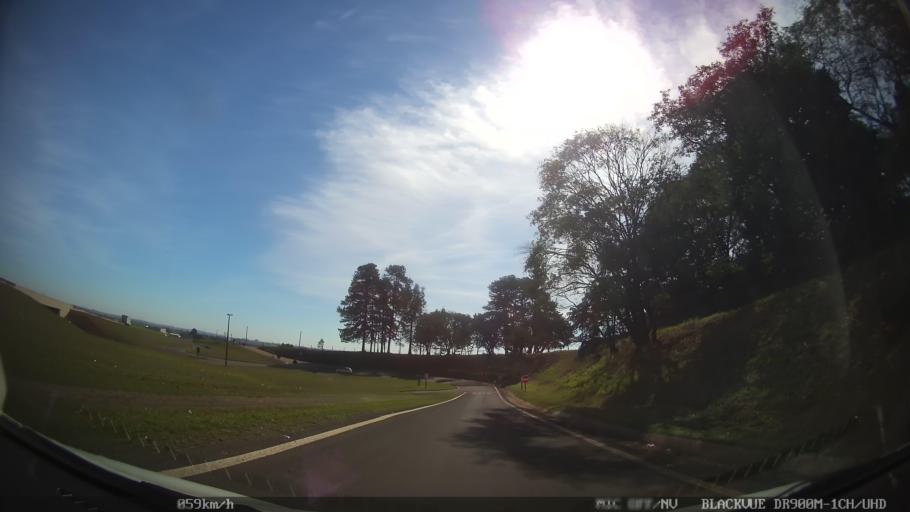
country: BR
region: Sao Paulo
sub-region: Leme
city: Leme
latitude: -22.1483
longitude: -47.4021
